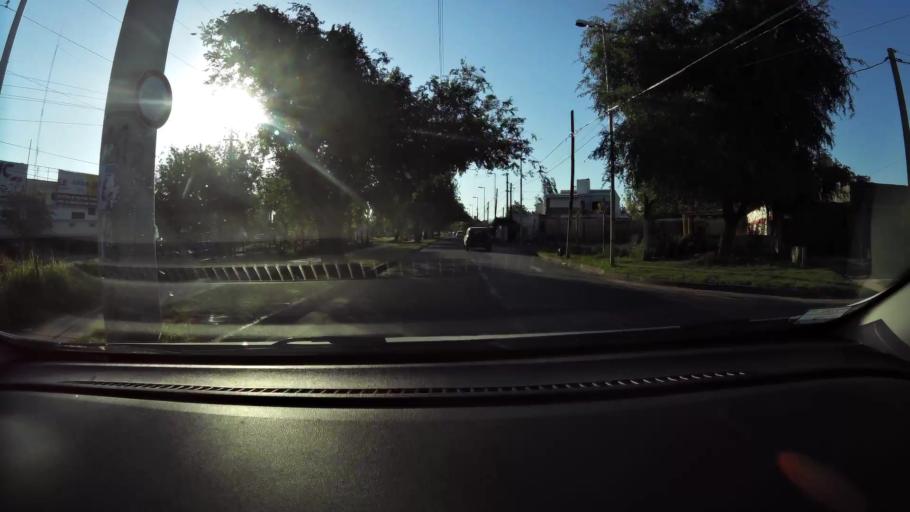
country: AR
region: Cordoba
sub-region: Departamento de Capital
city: Cordoba
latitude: -31.3714
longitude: -64.2026
